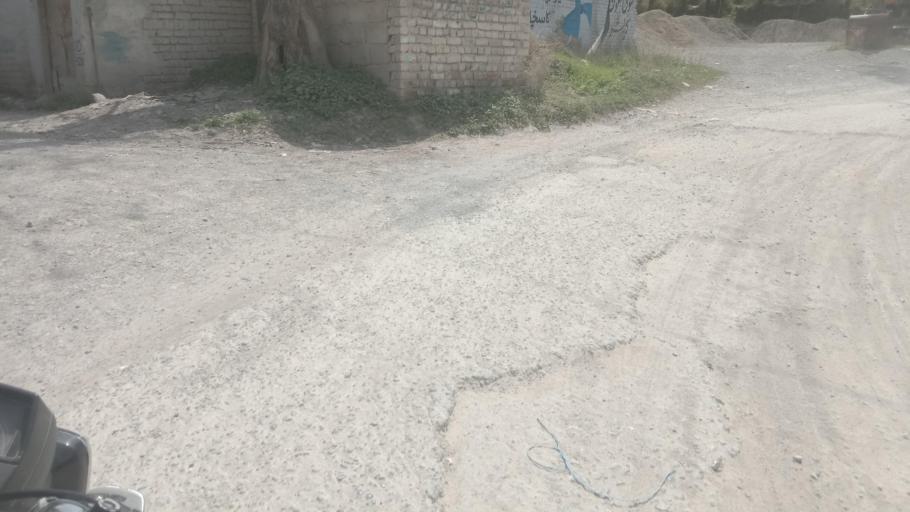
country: PK
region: Khyber Pakhtunkhwa
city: Abbottabad
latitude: 34.1621
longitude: 73.2754
